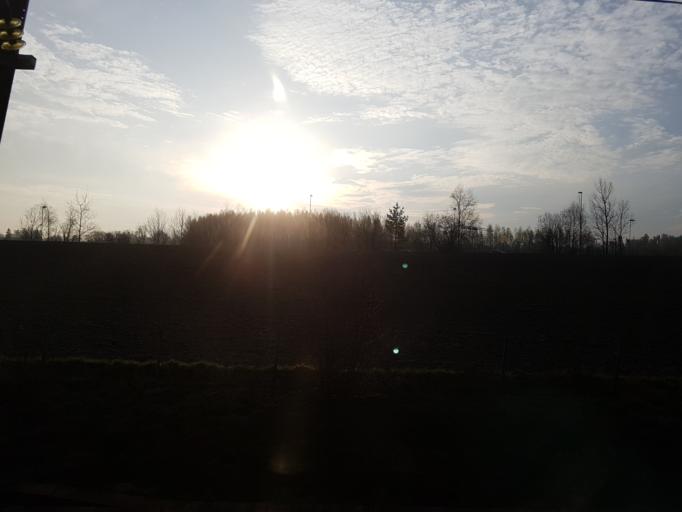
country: NO
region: Akershus
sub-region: Ullensaker
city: Jessheim
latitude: 60.1314
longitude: 11.1588
